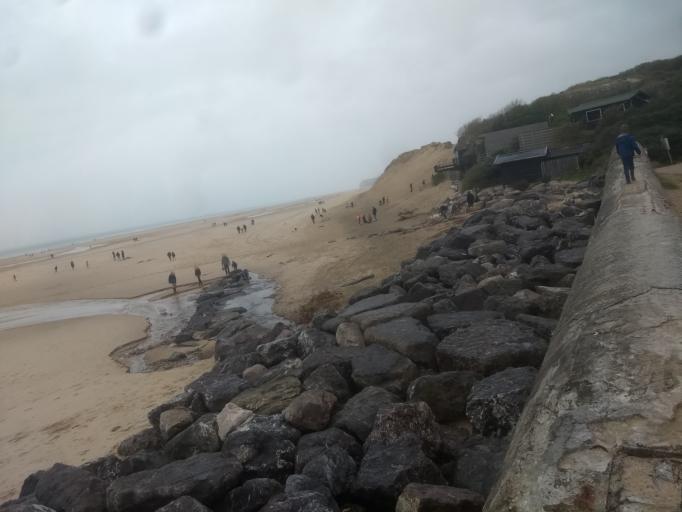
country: FR
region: Nord-Pas-de-Calais
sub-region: Departement du Pas-de-Calais
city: Wissant
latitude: 50.8876
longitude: 1.6603
